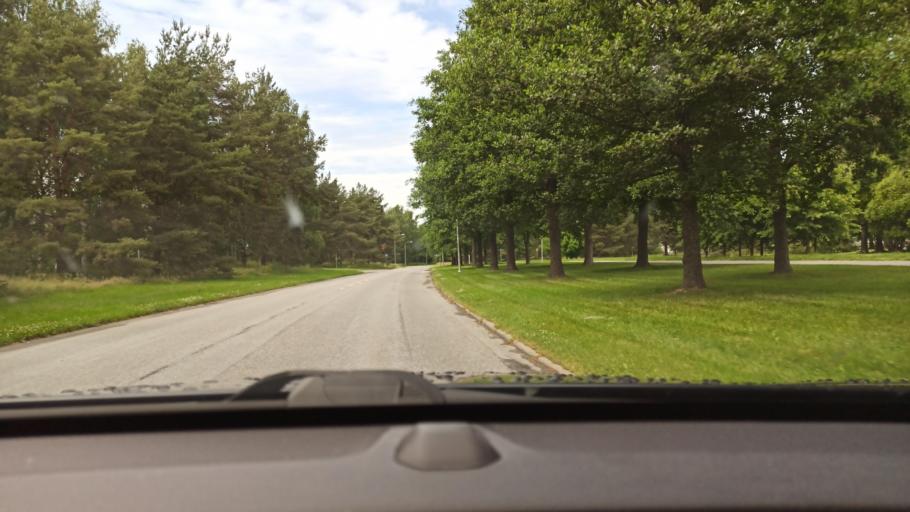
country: FI
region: Satakunta
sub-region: Pori
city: Pori
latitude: 61.5062
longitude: 21.7773
